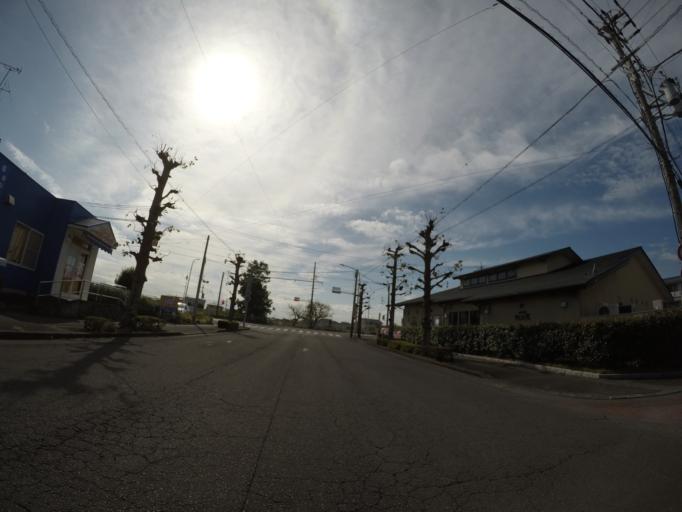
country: JP
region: Shizuoka
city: Yaizu
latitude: 34.8542
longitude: 138.3046
